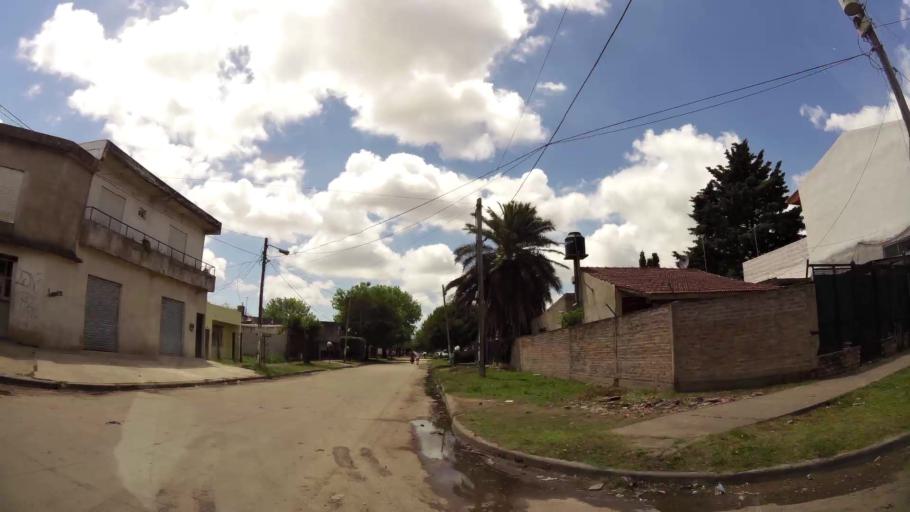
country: AR
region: Buenos Aires
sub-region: Partido de Quilmes
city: Quilmes
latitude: -34.8289
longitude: -58.2416
